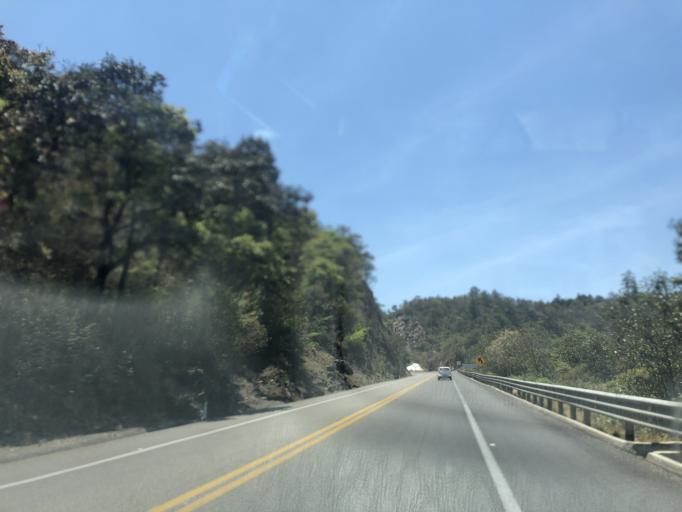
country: MX
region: Chiapas
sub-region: Zinacantan
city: Bochojbo Alto
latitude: 16.7166
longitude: -92.6814
